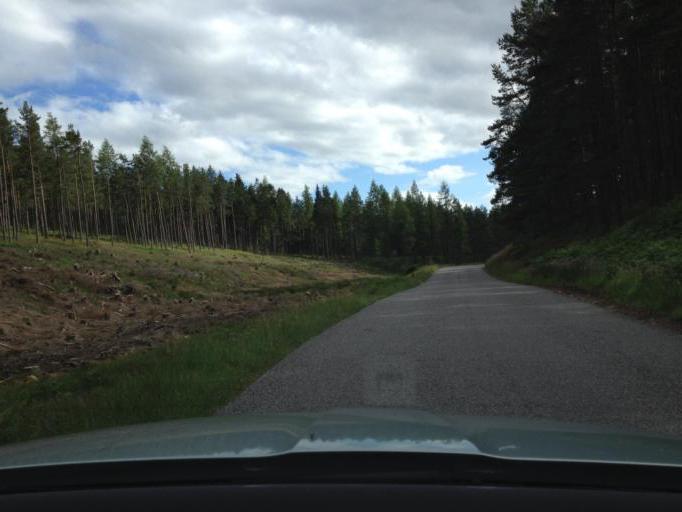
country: GB
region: Scotland
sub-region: Aberdeenshire
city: Banchory
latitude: 56.9984
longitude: -2.5723
